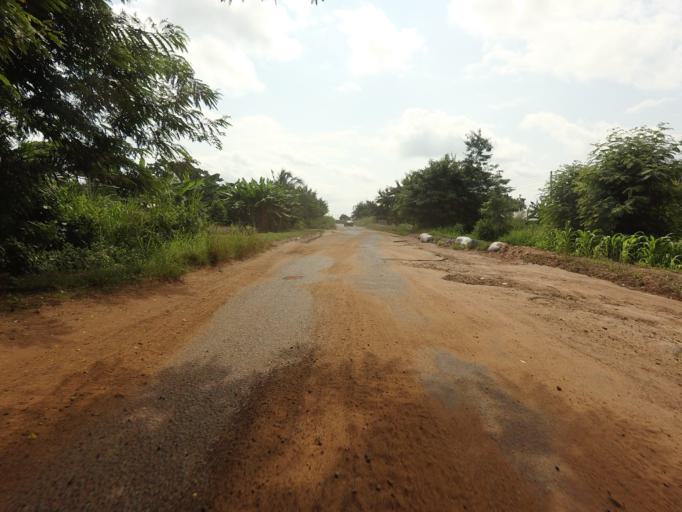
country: TG
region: Maritime
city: Lome
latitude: 6.2662
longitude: 0.9513
